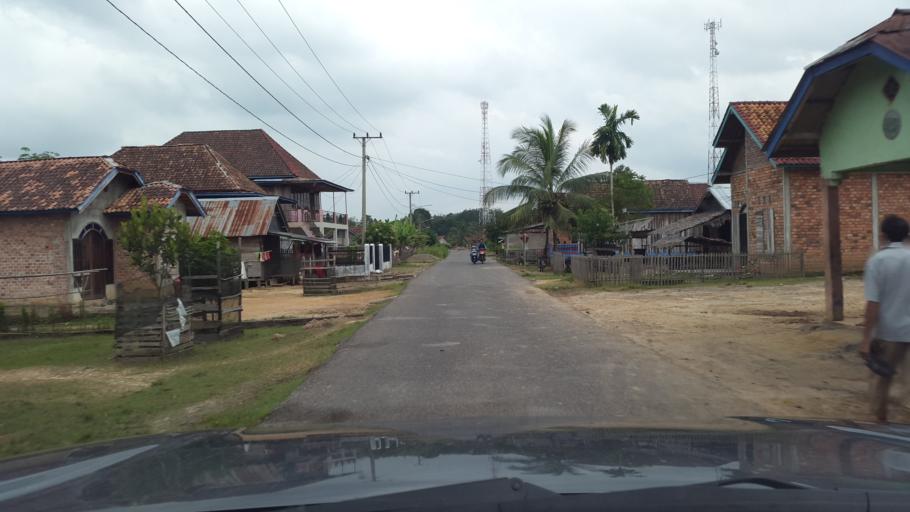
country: ID
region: South Sumatra
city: Gunungmenang
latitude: -3.1081
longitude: 103.9461
